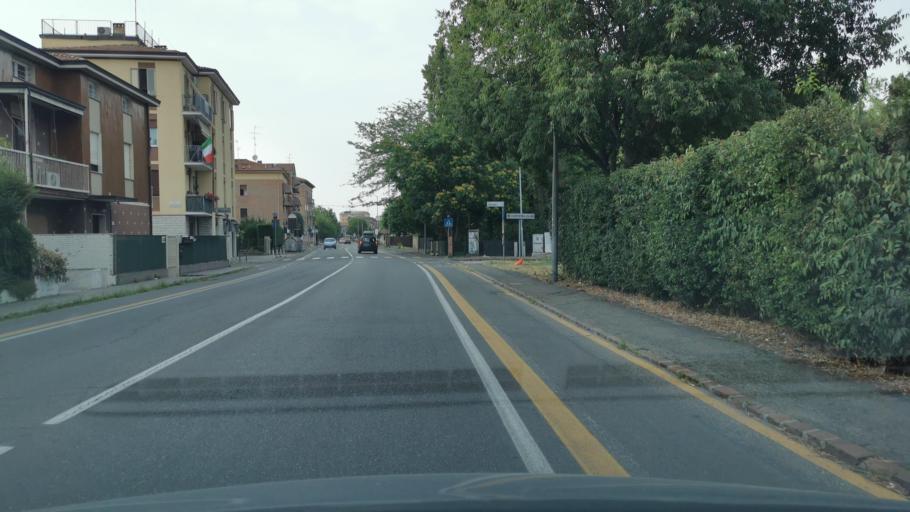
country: IT
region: Emilia-Romagna
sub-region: Provincia di Modena
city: Modena
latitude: 44.6288
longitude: 10.9270
